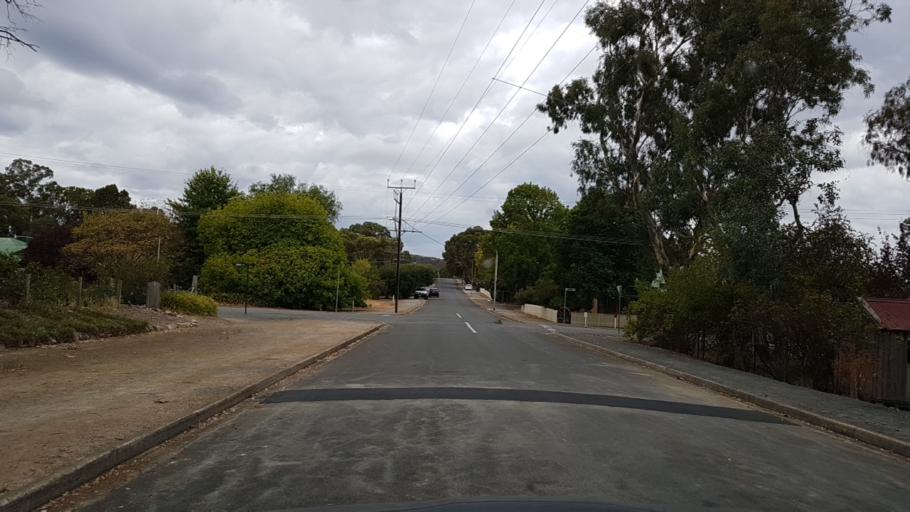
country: AU
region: South Australia
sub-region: Adelaide Hills
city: Gumeracha
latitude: -34.7823
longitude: 138.8546
